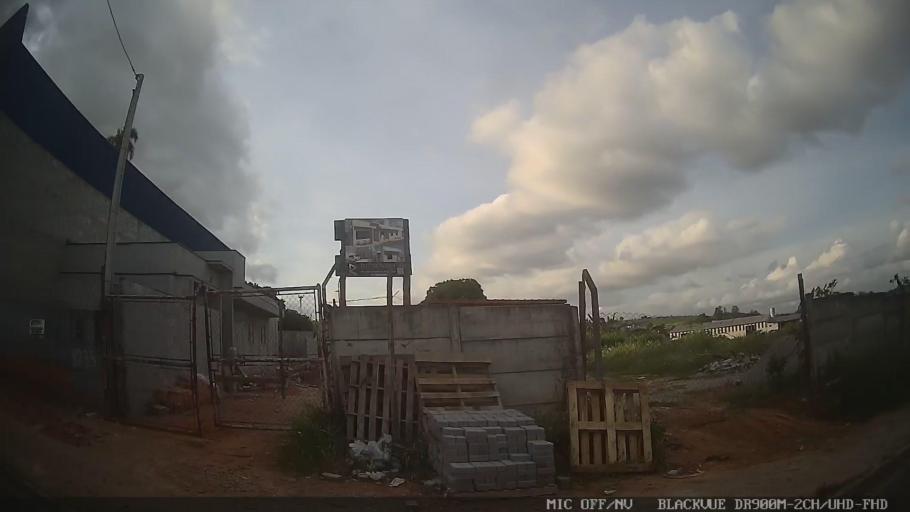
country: BR
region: Sao Paulo
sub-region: Atibaia
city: Atibaia
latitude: -23.1060
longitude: -46.5250
